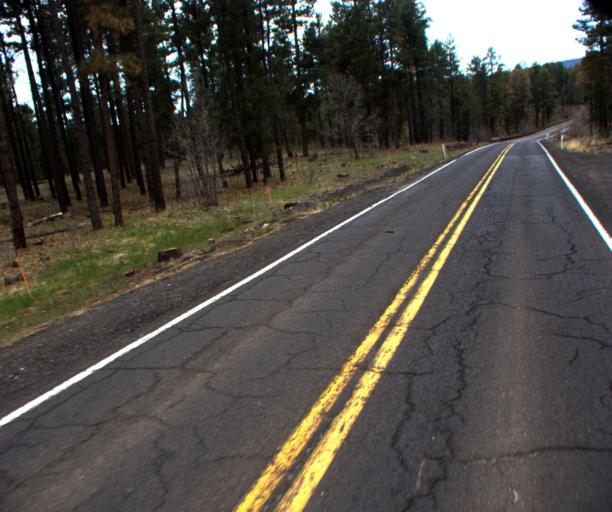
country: US
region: Arizona
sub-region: Coconino County
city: Kachina Village
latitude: 35.1124
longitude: -111.7144
